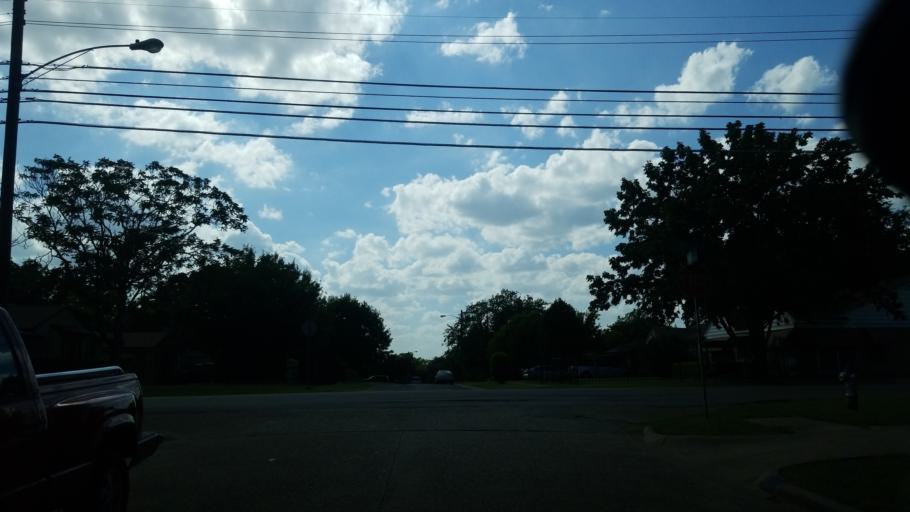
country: US
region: Texas
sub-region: Dallas County
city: Dallas
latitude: 32.7735
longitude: -96.7104
